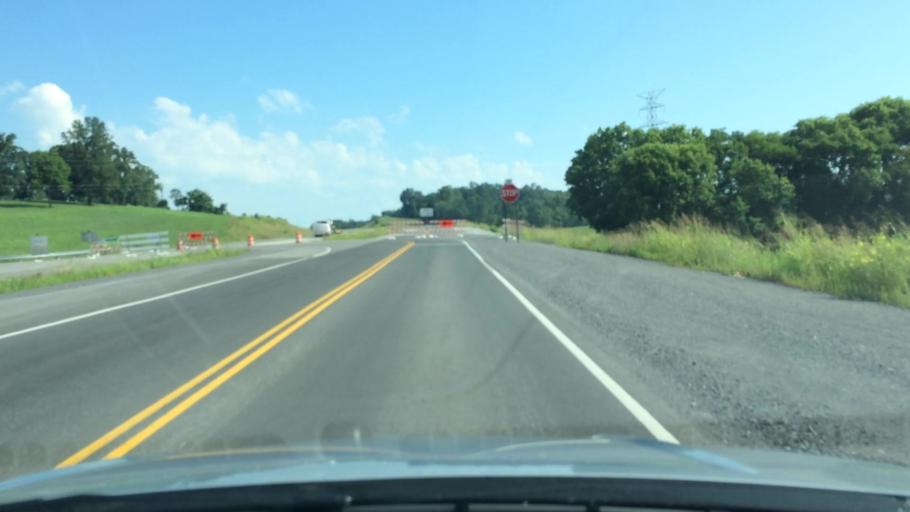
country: US
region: Tennessee
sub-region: Jefferson County
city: White Pine
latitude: 36.1486
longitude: -83.3430
